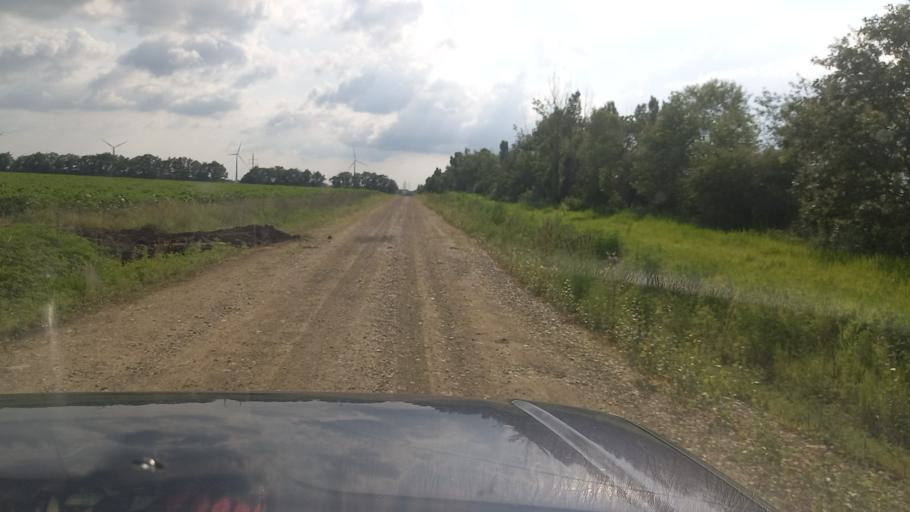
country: RU
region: Adygeya
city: Giaginskaya
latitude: 44.9475
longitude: 40.1232
